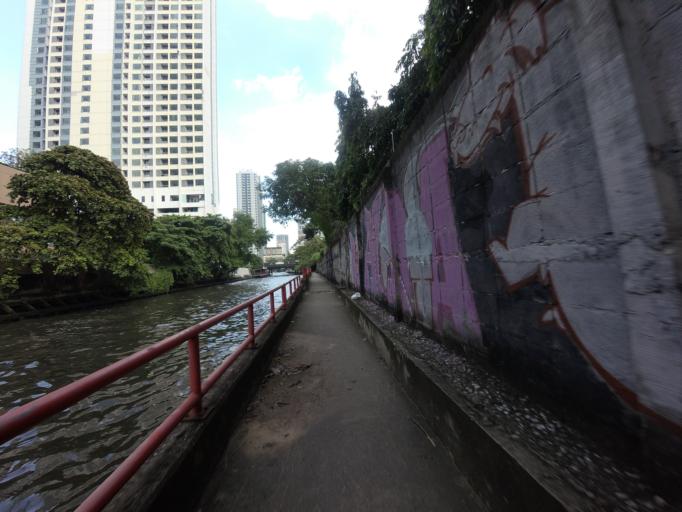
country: TH
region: Bangkok
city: Din Daeng
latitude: 13.7480
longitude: 100.5616
